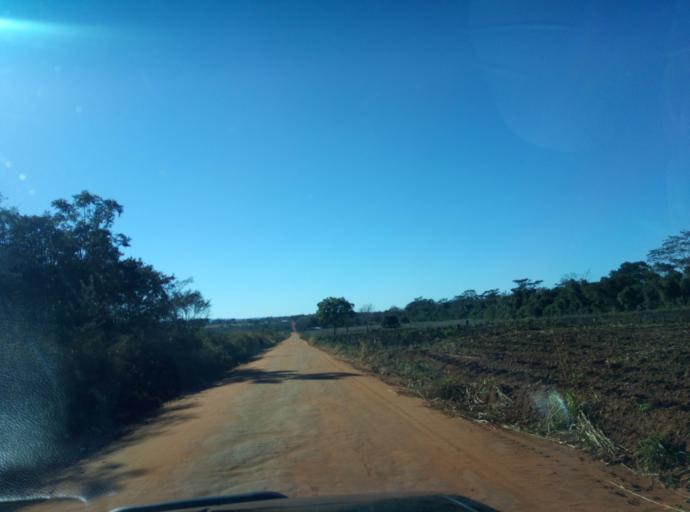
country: PY
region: Caaguazu
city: Doctor Cecilio Baez
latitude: -25.1622
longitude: -56.2687
